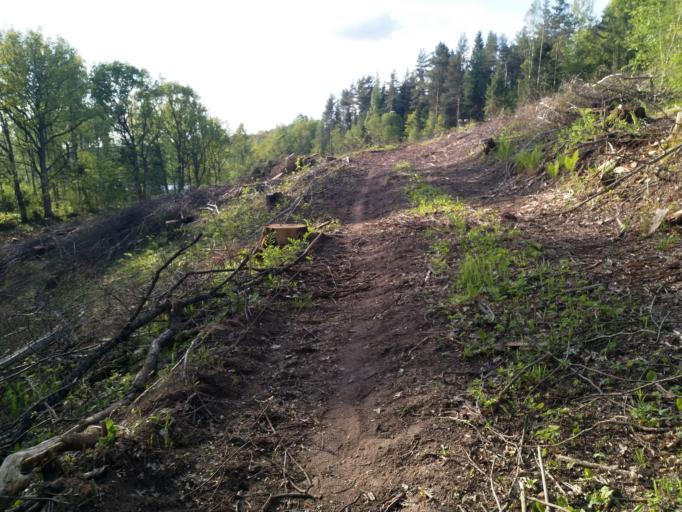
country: LV
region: Kuldigas Rajons
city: Kuldiga
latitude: 56.8591
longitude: 21.8593
